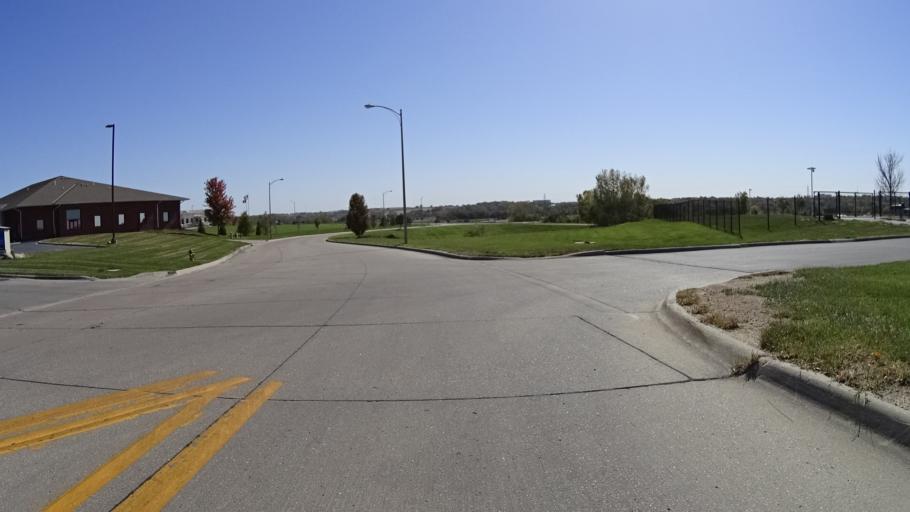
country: US
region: Nebraska
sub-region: Sarpy County
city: Papillion
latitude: 41.1611
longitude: -96.0277
